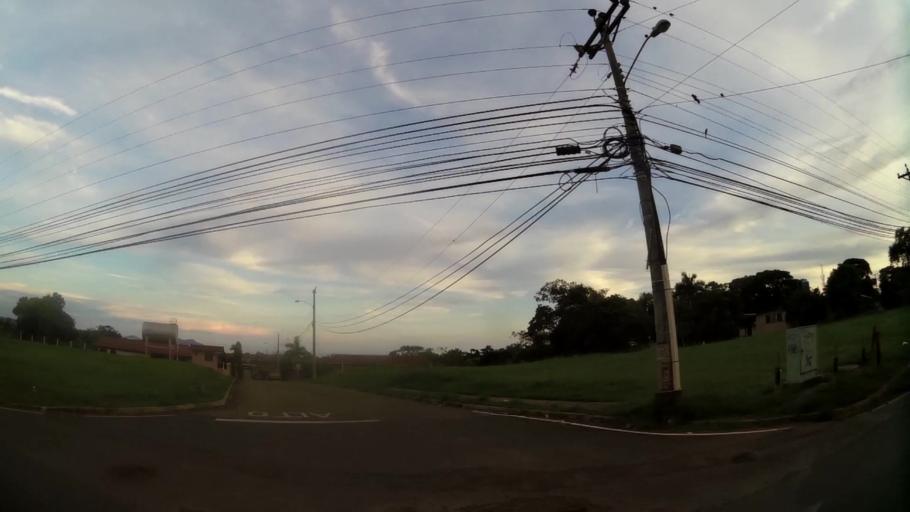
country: PA
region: Panama
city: La Chorrera
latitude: 8.8651
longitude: -79.7653
